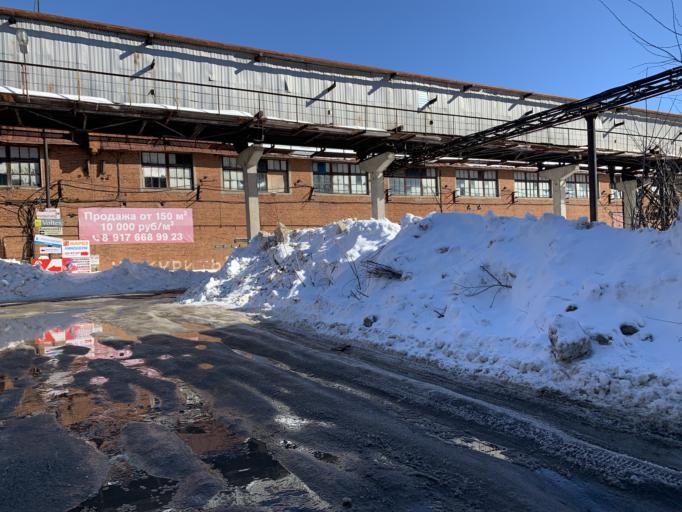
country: RU
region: Chuvashia
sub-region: Cheboksarskiy Rayon
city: Cheboksary
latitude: 56.1423
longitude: 47.2782
